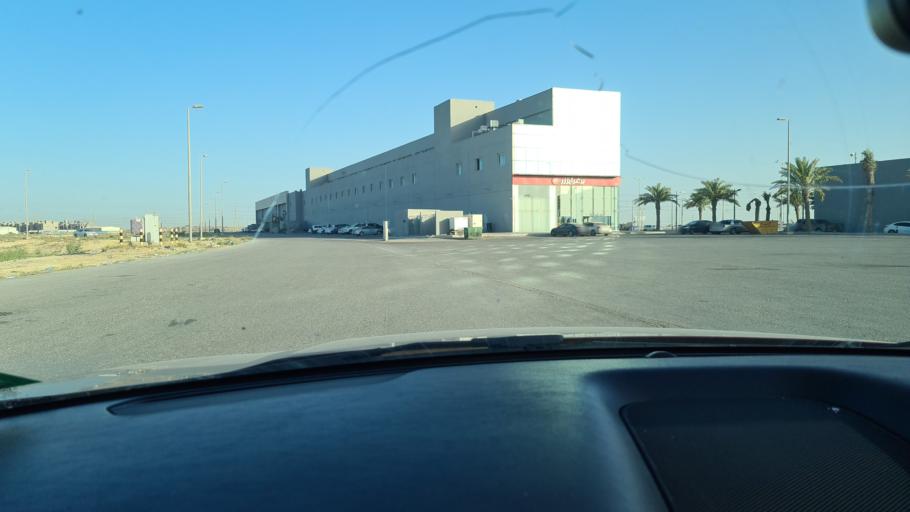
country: SA
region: Eastern Province
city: Al Jubayl
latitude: 26.9264
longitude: 49.7141
